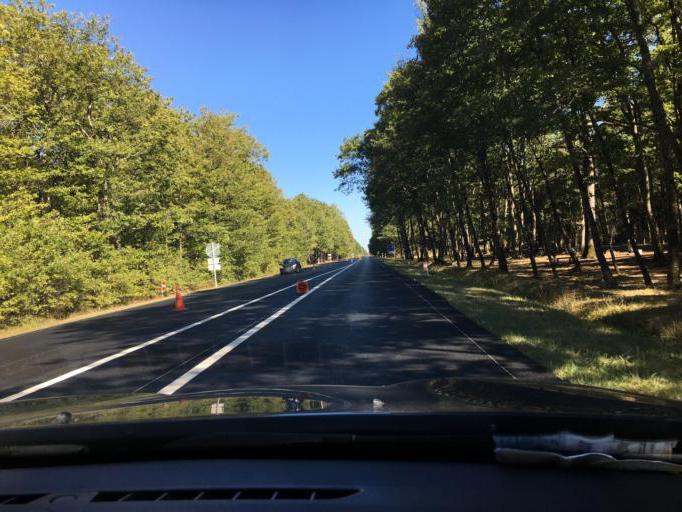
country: FR
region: Centre
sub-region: Departement d'Indre-et-Loire
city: Azay-le-Rideau
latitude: 47.2833
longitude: 0.5113
